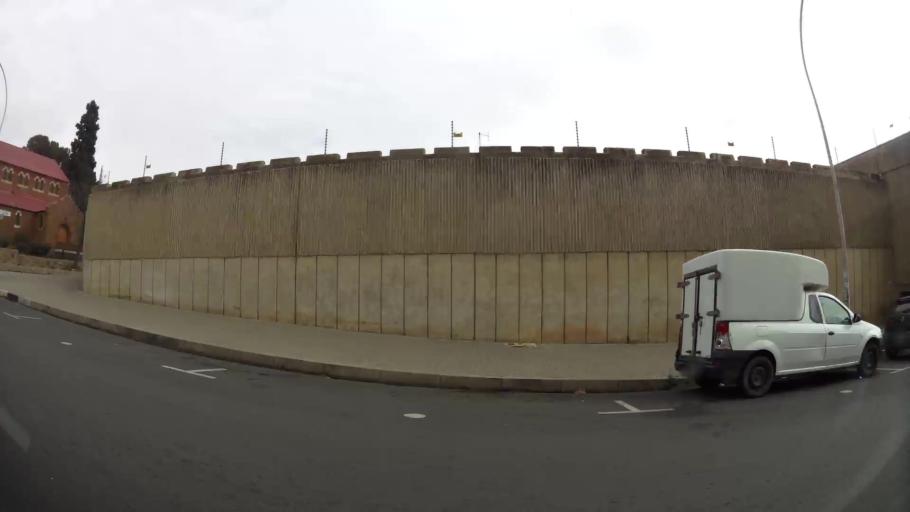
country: ZA
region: Orange Free State
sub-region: Mangaung Metropolitan Municipality
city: Bloemfontein
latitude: -29.1206
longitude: 26.2196
